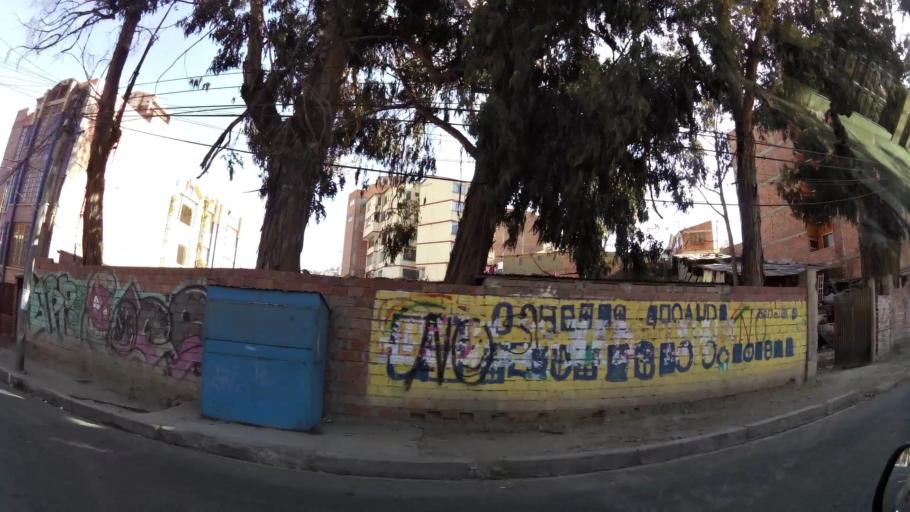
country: BO
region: La Paz
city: La Paz
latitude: -16.5173
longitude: -68.1268
